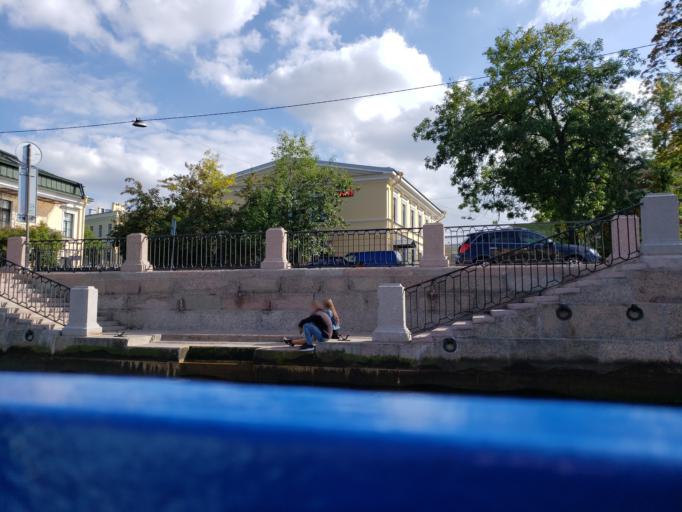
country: RU
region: St.-Petersburg
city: Saint Petersburg
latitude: 59.9205
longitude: 30.3138
